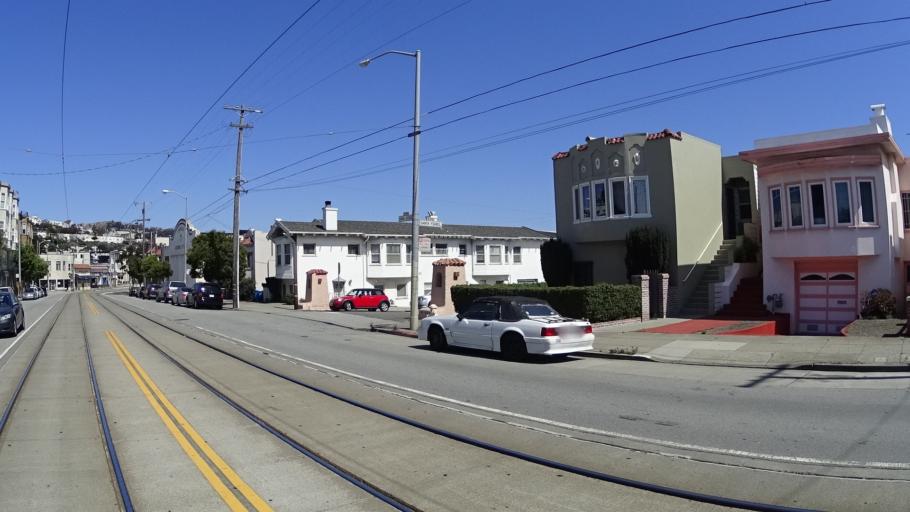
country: US
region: California
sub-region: San Mateo County
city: Daly City
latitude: 37.7280
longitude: -122.4408
